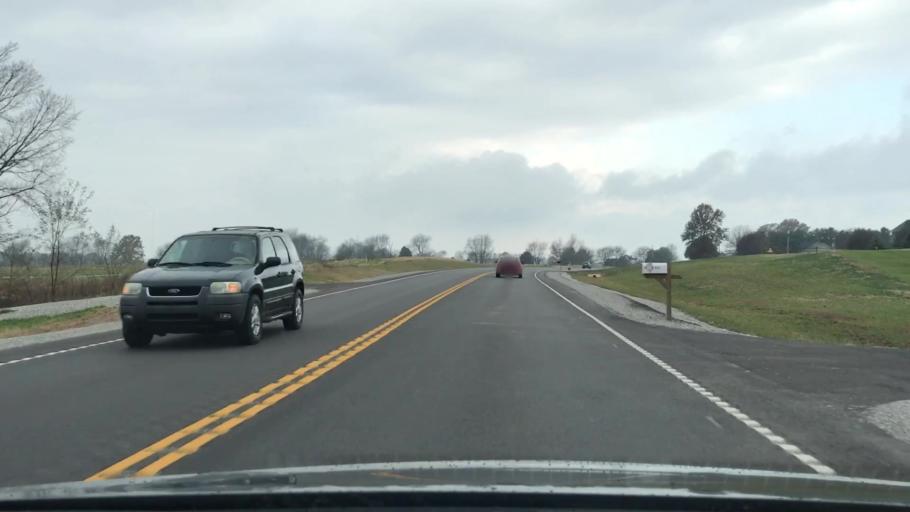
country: US
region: Kentucky
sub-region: Simpson County
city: Franklin
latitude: 36.7097
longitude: -86.4949
